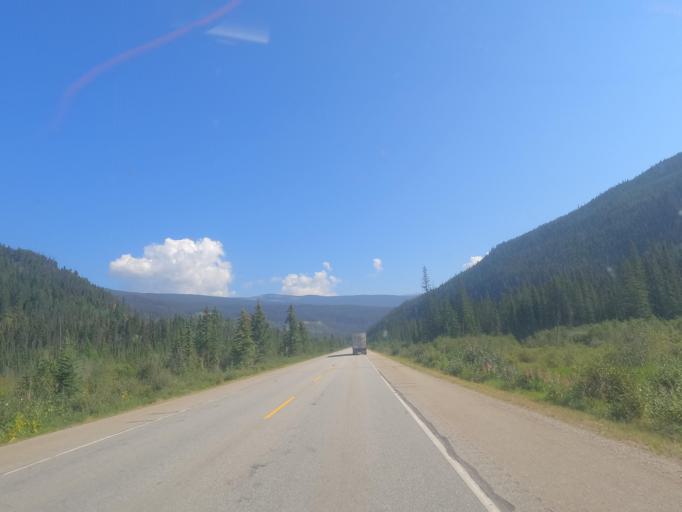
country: CA
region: Alberta
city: Jasper Park Lodge
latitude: 52.8793
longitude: -118.4921
